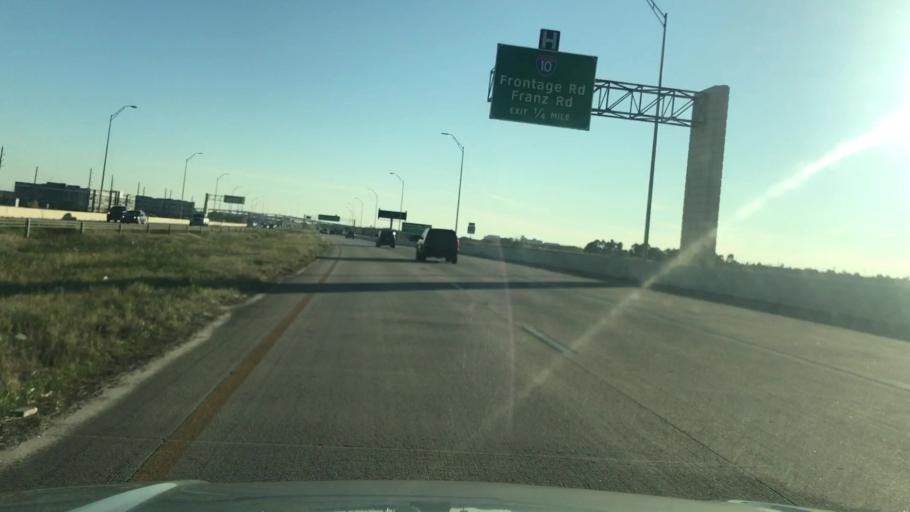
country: US
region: Texas
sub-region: Harris County
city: Katy
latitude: 29.8120
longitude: -95.7736
